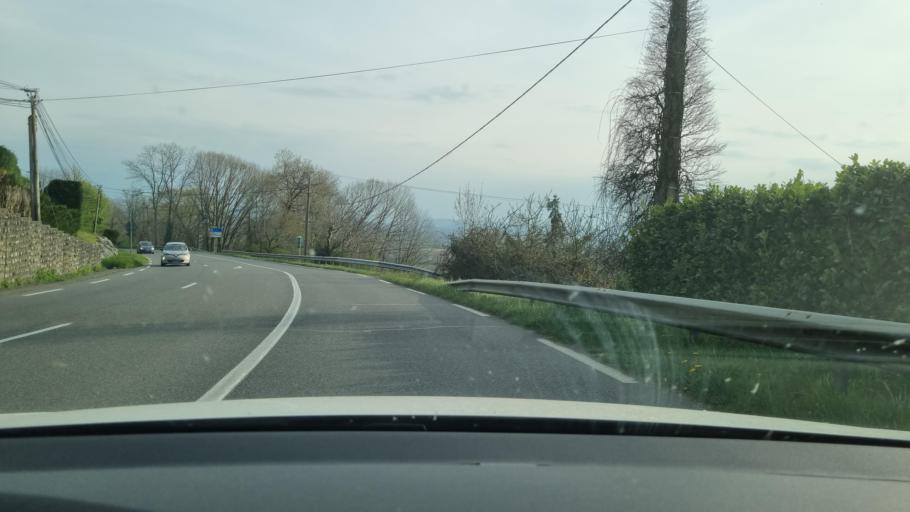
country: FR
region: Aquitaine
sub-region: Departement des Pyrenees-Atlantiques
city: Morlaas
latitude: 43.3346
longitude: -0.2784
